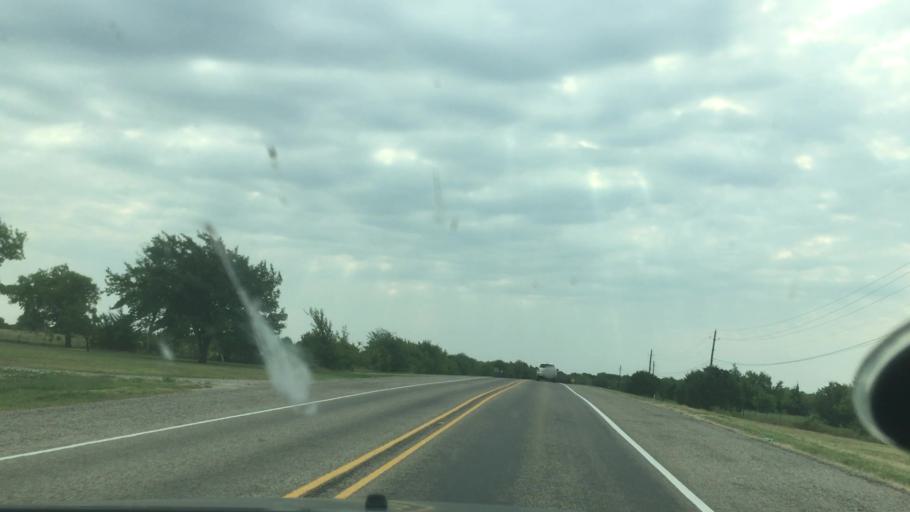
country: US
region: Texas
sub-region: Grayson County
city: Pottsboro
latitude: 33.7991
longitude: -96.6476
